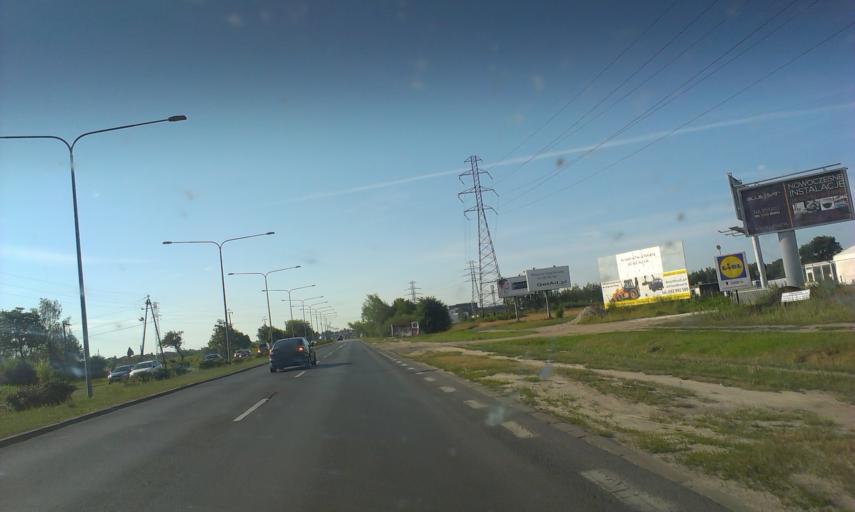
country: PL
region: Masovian Voivodeship
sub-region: Powiat piaseczynski
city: Konstancin-Jeziorna
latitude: 52.1159
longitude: 21.1071
